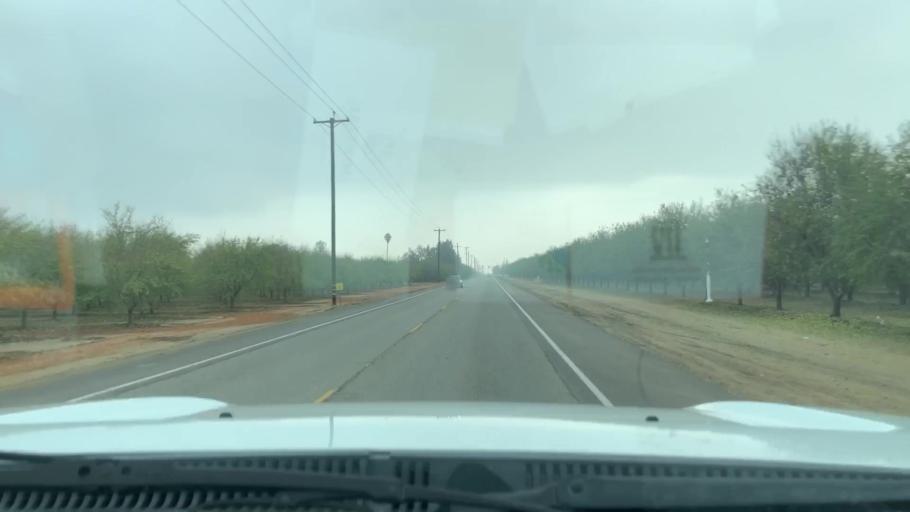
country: US
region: California
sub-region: Kern County
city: Wasco
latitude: 35.5580
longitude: -119.3384
